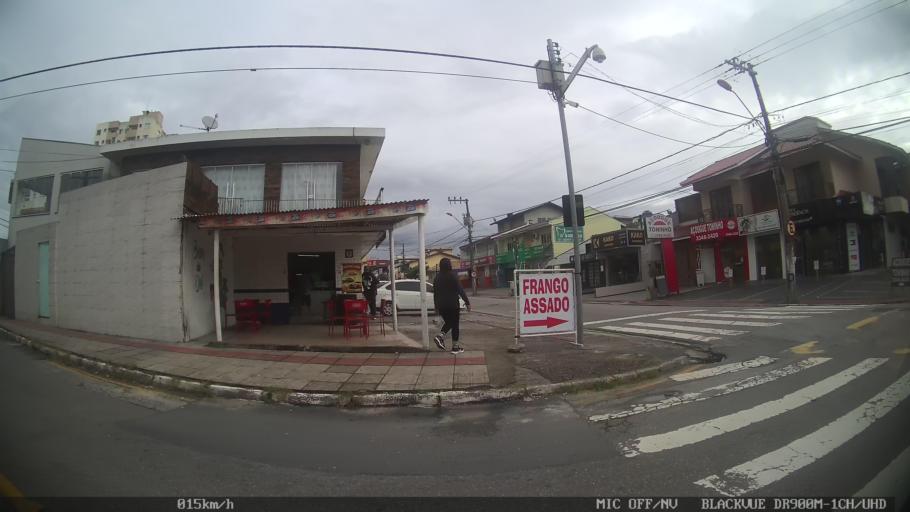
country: BR
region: Santa Catarina
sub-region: Sao Jose
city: Campinas
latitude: -27.5557
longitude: -48.6232
